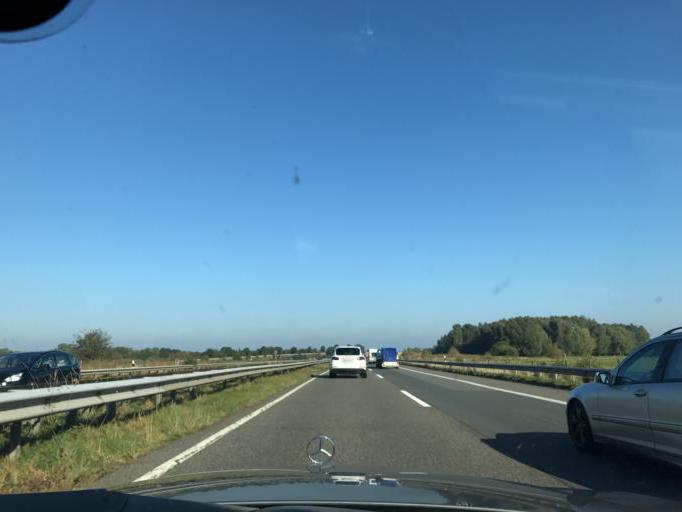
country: DE
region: Lower Saxony
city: Leer
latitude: 53.2560
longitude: 7.4386
